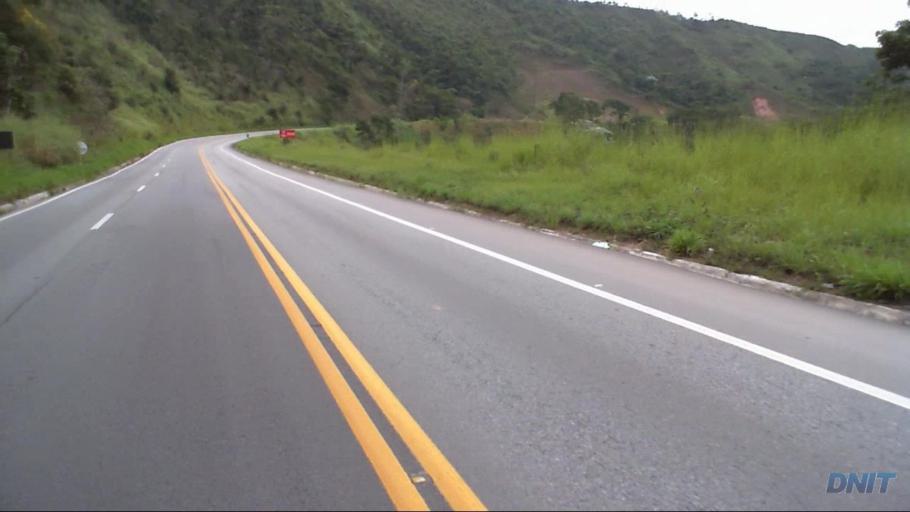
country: BR
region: Minas Gerais
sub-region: Nova Era
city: Nova Era
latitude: -19.6366
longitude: -42.8992
